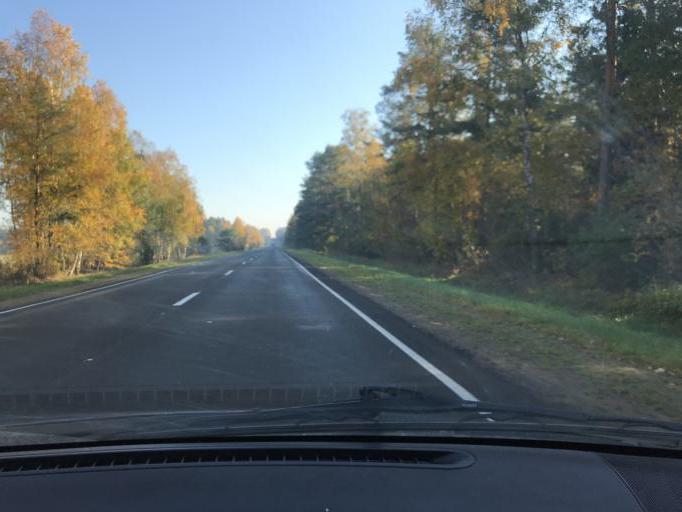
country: BY
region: Brest
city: Baranovichi
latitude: 52.9269
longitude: 26.0129
